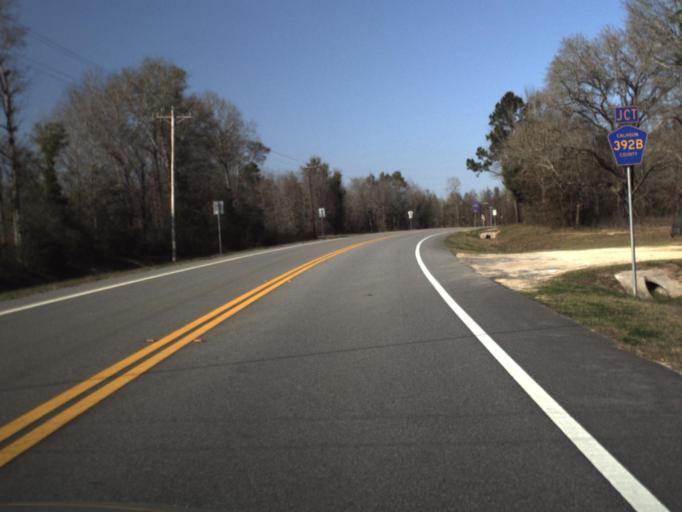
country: US
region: Florida
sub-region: Gulf County
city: Wewahitchka
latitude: 30.2873
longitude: -85.2417
